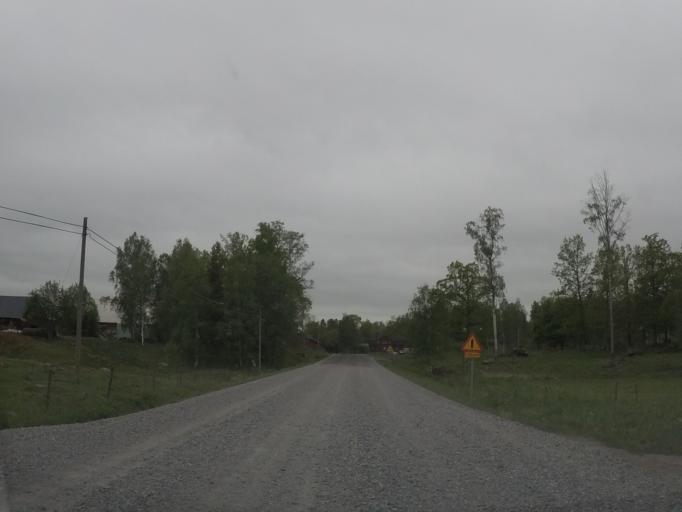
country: SE
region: Soedermanland
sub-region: Flens Kommun
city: Halleforsnas
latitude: 59.1658
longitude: 16.5103
